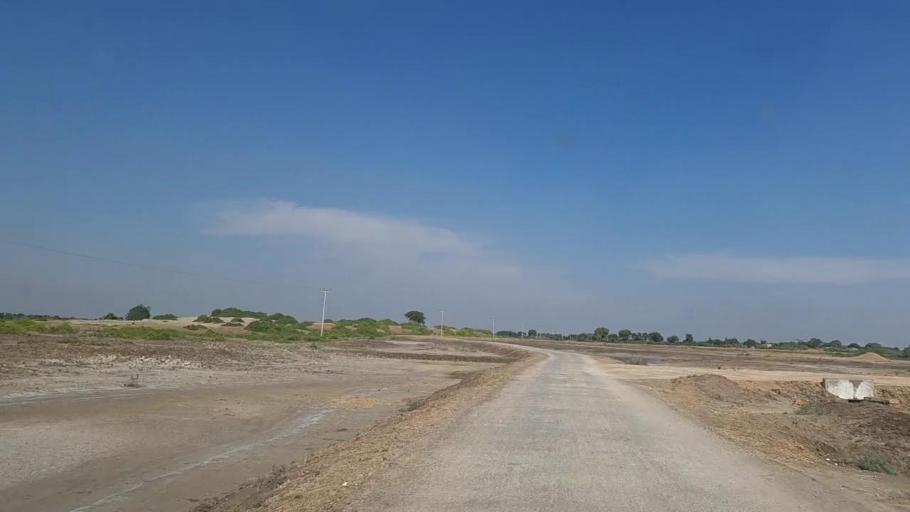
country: PK
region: Sindh
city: Mirpur Batoro
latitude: 24.7453
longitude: 68.2759
